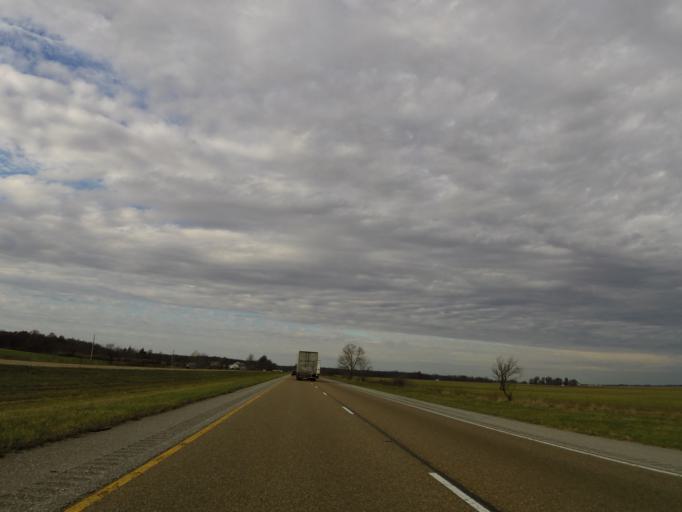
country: US
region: Illinois
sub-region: Washington County
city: Nashville
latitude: 38.3913
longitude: -89.2802
